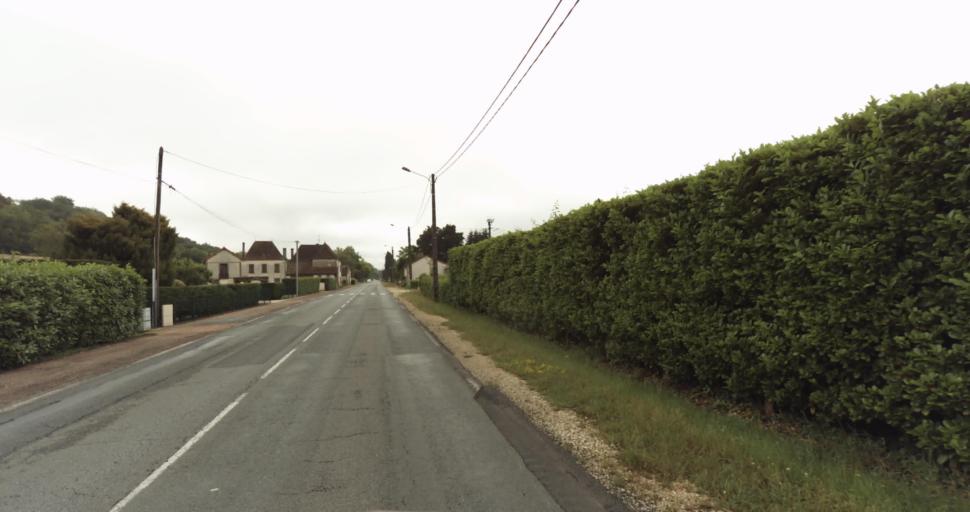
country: FR
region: Aquitaine
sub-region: Departement de la Dordogne
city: Mouleydier
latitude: 44.8534
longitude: 0.6053
